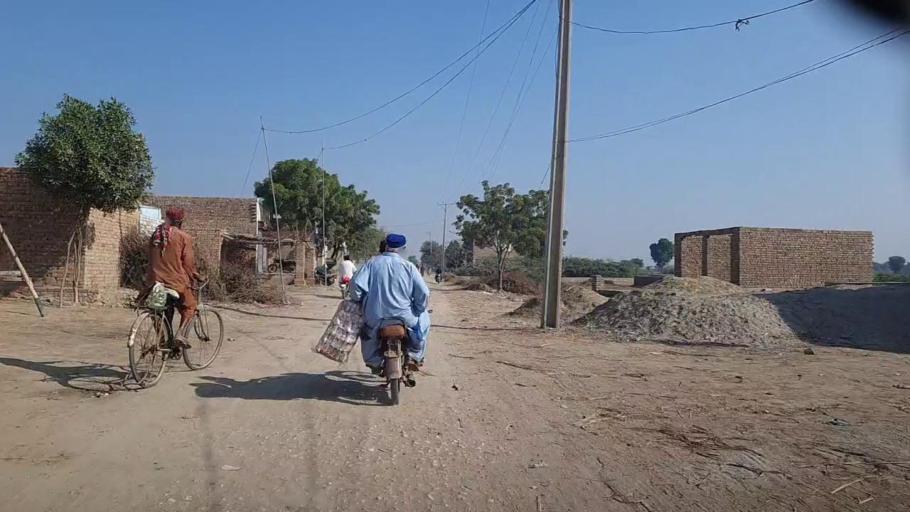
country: PK
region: Sindh
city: Darya Khan Marri
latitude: 26.6738
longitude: 68.3137
